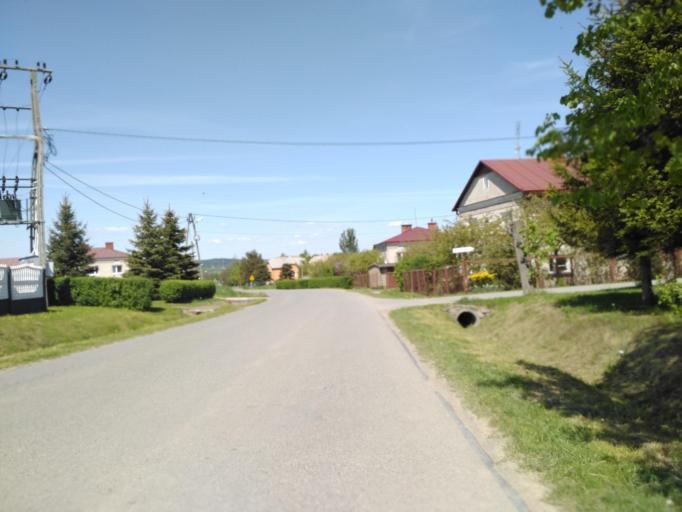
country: PL
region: Subcarpathian Voivodeship
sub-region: Powiat krosnienski
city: Dukla
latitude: 49.5449
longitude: 21.7284
